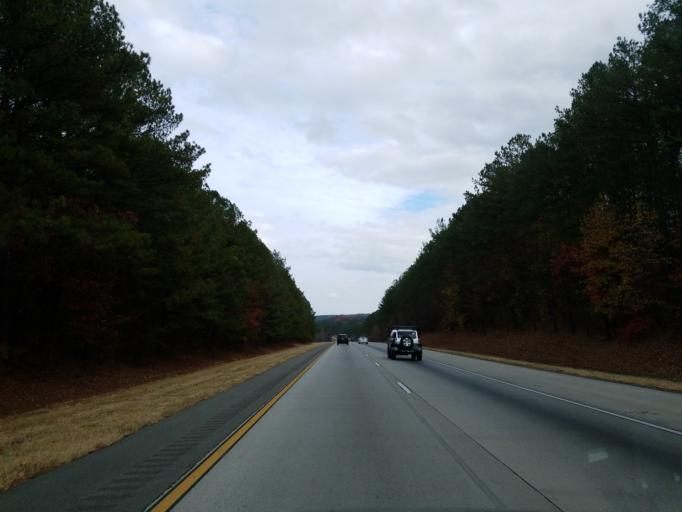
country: US
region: Georgia
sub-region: Carroll County
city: Mount Zion
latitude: 33.6872
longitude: -85.2366
